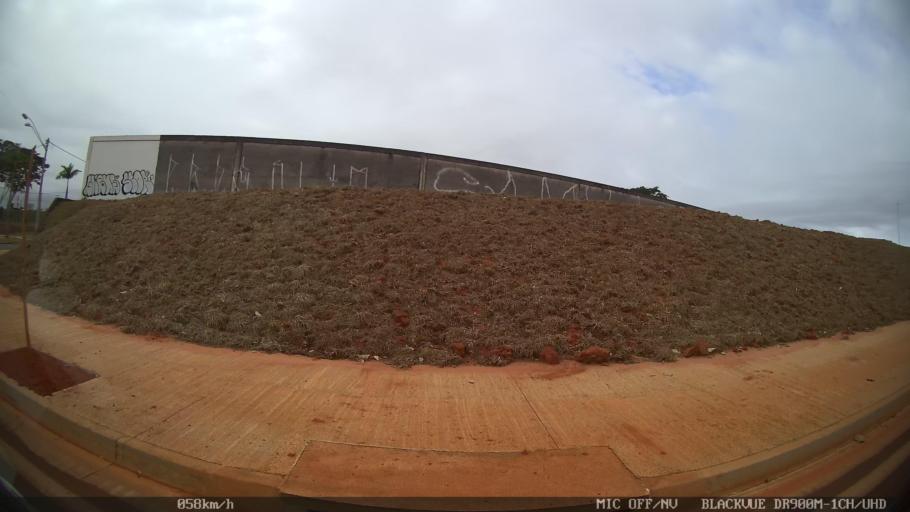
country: BR
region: Sao Paulo
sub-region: Sao Jose Do Rio Preto
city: Sao Jose do Rio Preto
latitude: -20.8241
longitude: -49.4193
